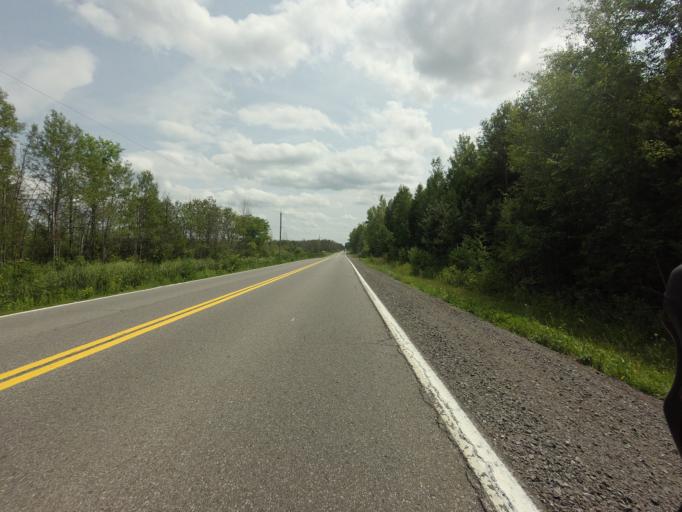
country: CA
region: Ontario
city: Ottawa
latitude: 45.2204
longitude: -75.6029
